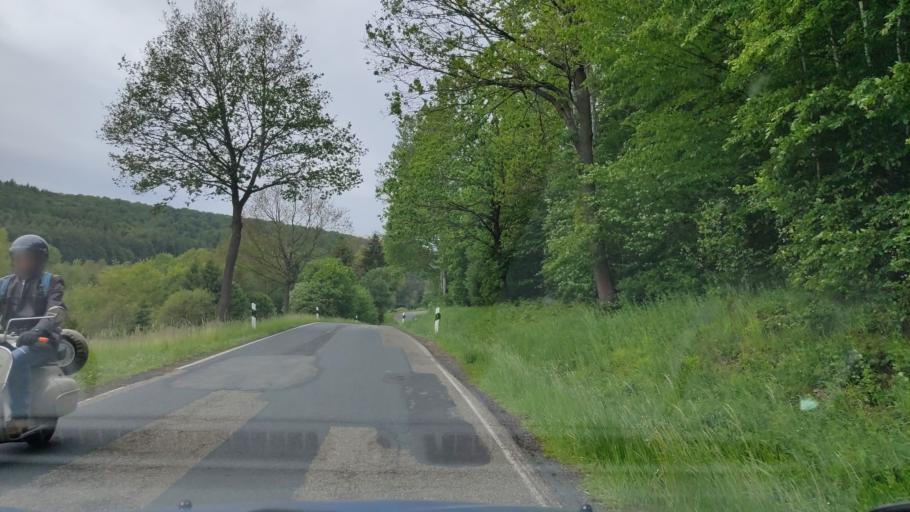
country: DE
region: Lower Saxony
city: Hardegsen
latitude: 51.7017
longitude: 9.7374
